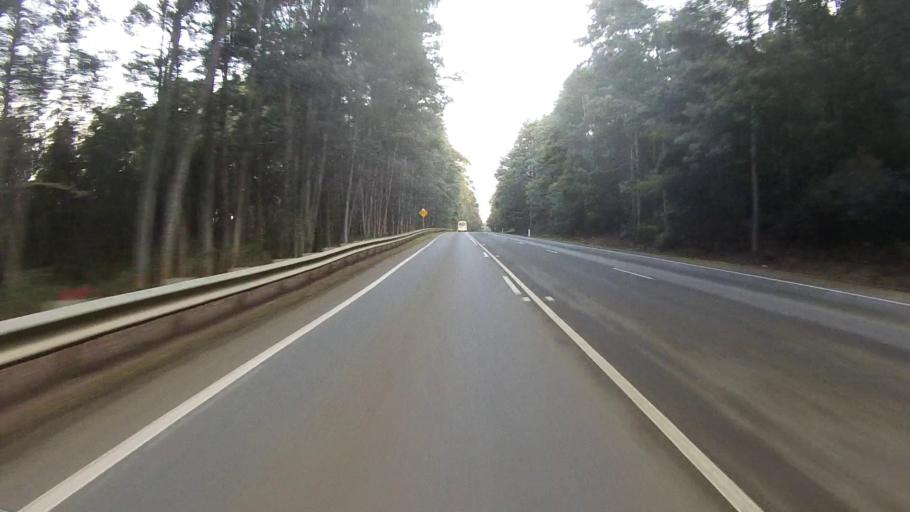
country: AU
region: Tasmania
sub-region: Sorell
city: Sorell
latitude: -43.0057
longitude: 147.9267
